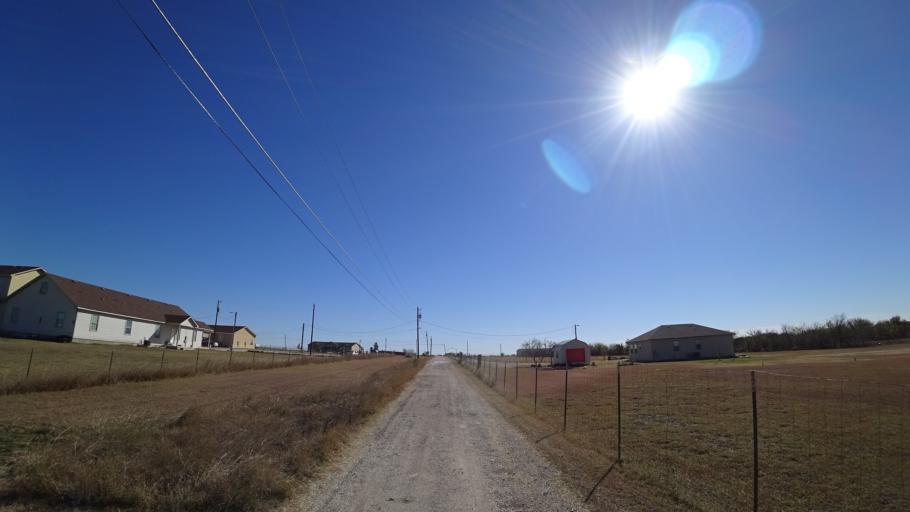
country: US
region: Texas
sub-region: Travis County
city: Garfield
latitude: 30.0979
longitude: -97.6205
